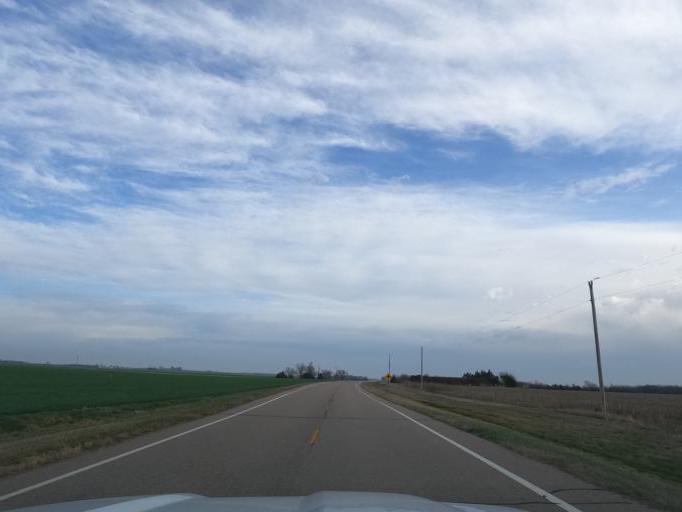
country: US
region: Kansas
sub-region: Reno County
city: Nickerson
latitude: 38.0550
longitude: -98.1790
